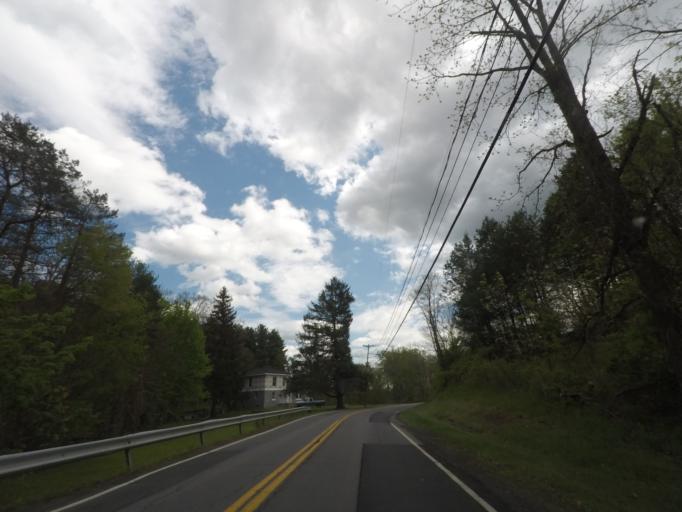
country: US
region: New York
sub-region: Albany County
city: Westmere
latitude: 42.6997
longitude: -73.9122
